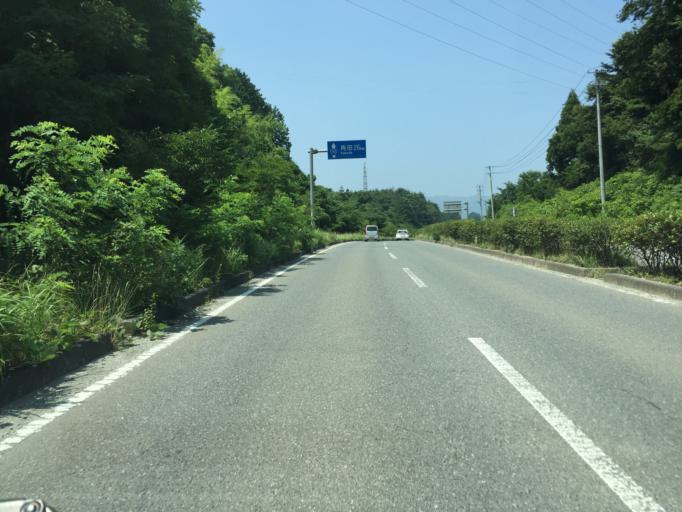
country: JP
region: Miyagi
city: Marumori
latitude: 37.8374
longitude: 140.9162
